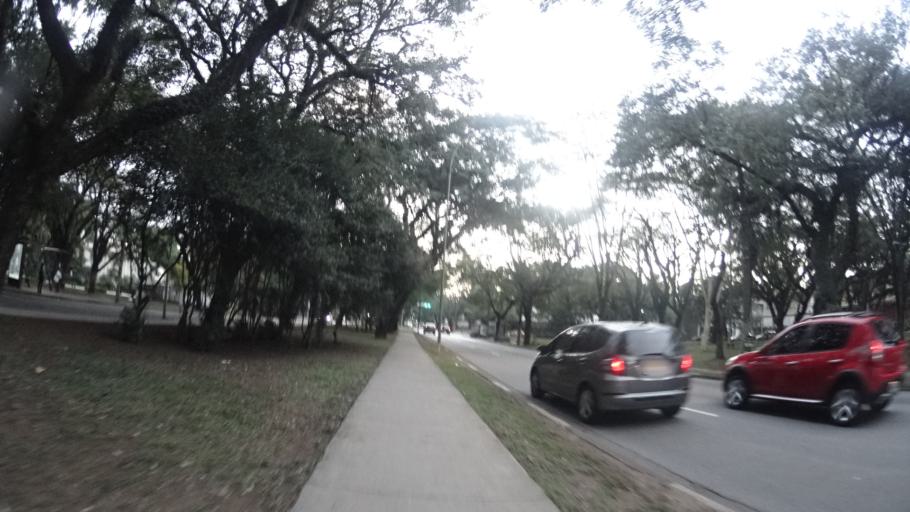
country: BR
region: Sao Paulo
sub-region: Sao Paulo
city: Sao Paulo
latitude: -23.5574
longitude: -46.7014
